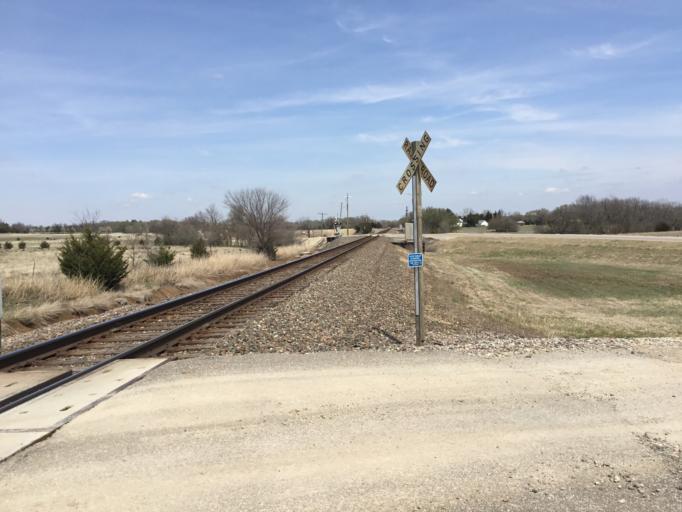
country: US
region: Kansas
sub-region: Butler County
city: Augusta
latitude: 37.6358
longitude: -97.0181
